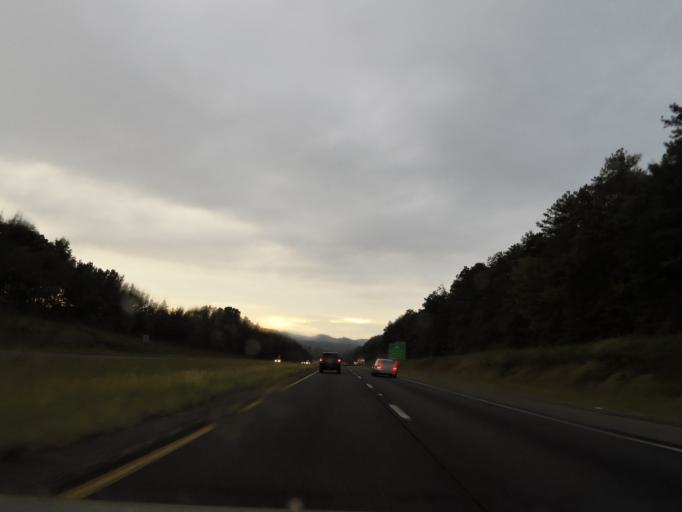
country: US
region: Alabama
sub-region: Saint Clair County
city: Springville
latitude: 33.7723
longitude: -86.4525
